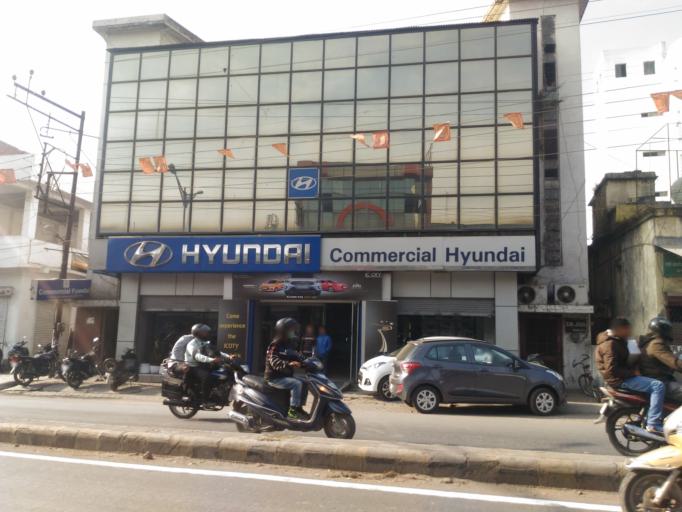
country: IN
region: Uttarakhand
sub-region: Dehradun
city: Dehradun
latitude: 30.3172
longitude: 78.0391
